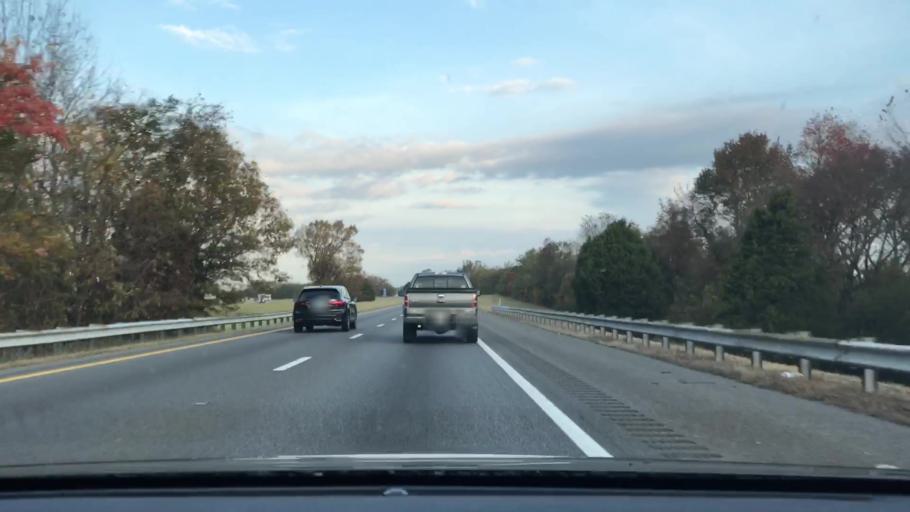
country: US
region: Tennessee
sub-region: Montgomery County
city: Clarksville
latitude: 36.6219
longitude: -87.3015
